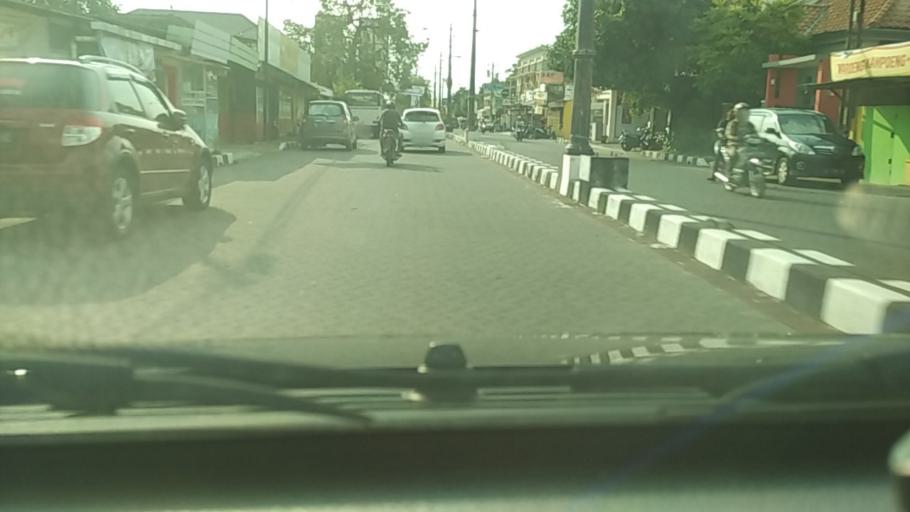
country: ID
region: Daerah Istimewa Yogyakarta
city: Yogyakarta
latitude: -7.7690
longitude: 110.3902
